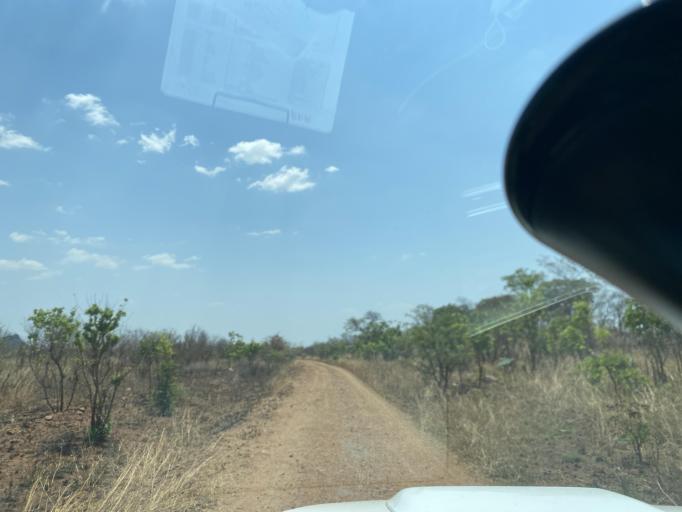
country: ZM
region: Lusaka
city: Lusaka
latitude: -15.5069
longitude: 27.9789
